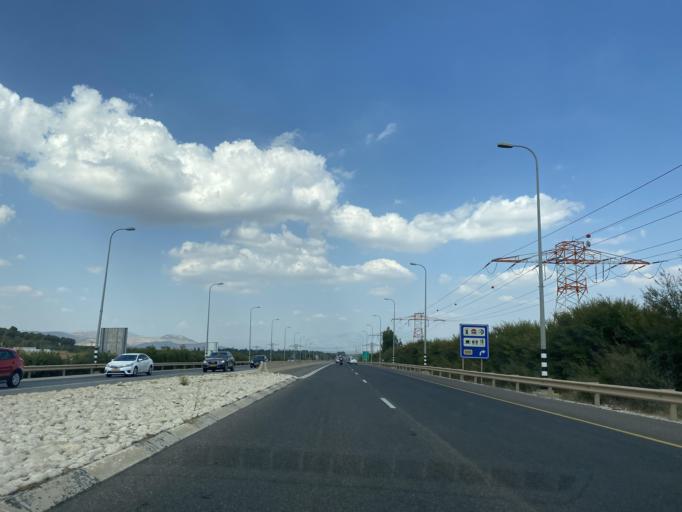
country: IL
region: Northern District
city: Rosh Pinna
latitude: 32.9840
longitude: 35.5586
